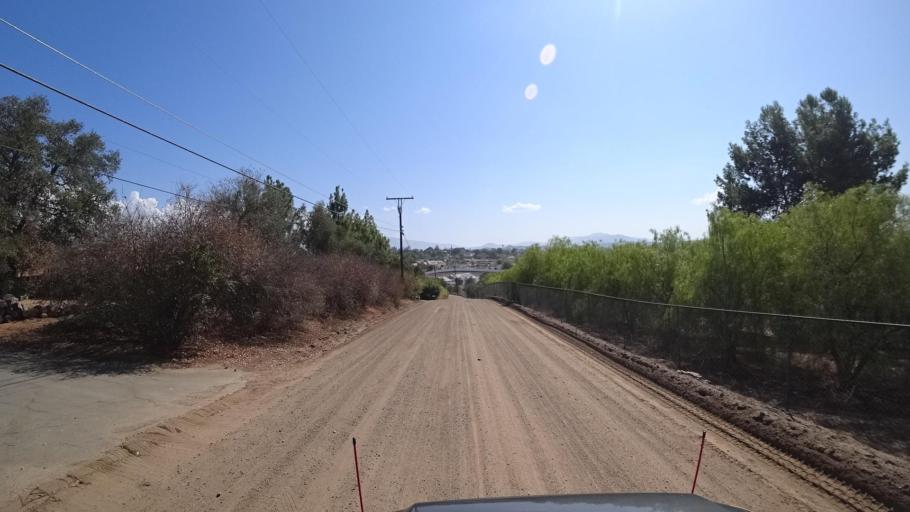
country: US
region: California
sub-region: San Diego County
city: Valley Center
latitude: 33.2811
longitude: -117.0364
